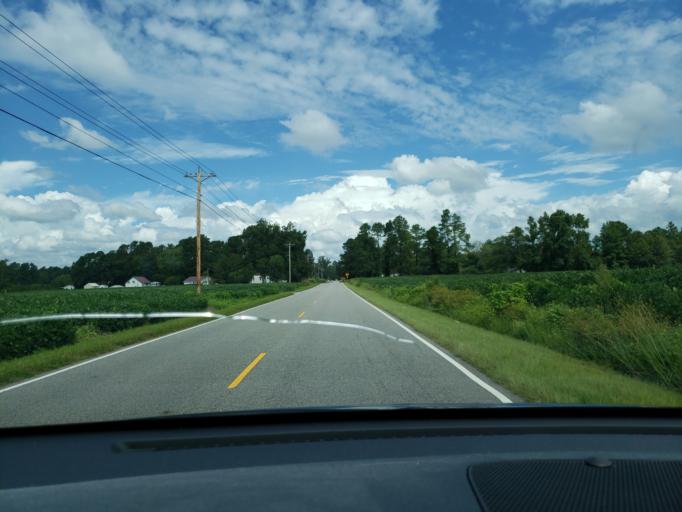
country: US
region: North Carolina
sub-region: Columbus County
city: Tabor City
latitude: 34.1831
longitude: -78.7884
